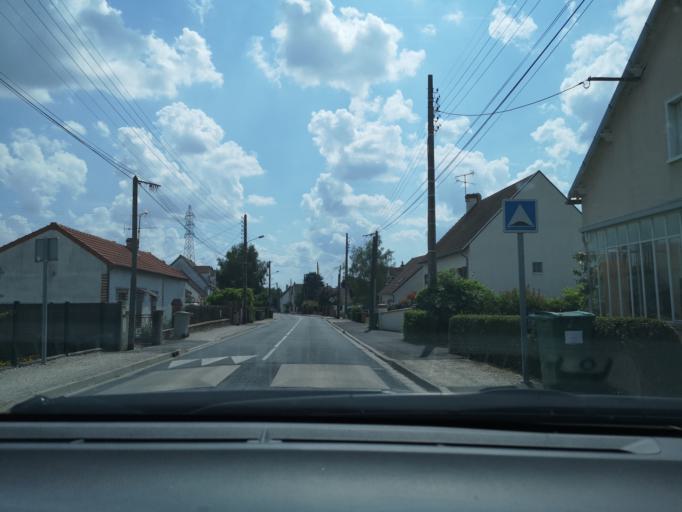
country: FR
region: Centre
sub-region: Departement du Loiret
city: Semoy
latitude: 47.9322
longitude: 1.9413
